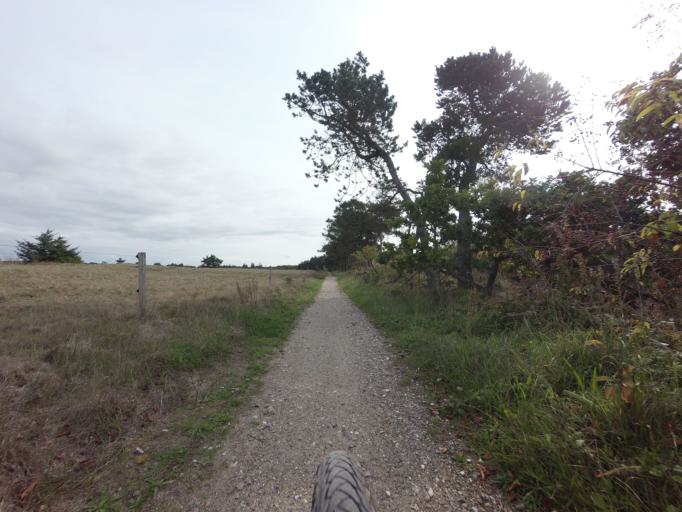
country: DK
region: North Denmark
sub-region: Hjorring Kommune
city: Sindal
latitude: 57.5854
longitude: 10.1732
